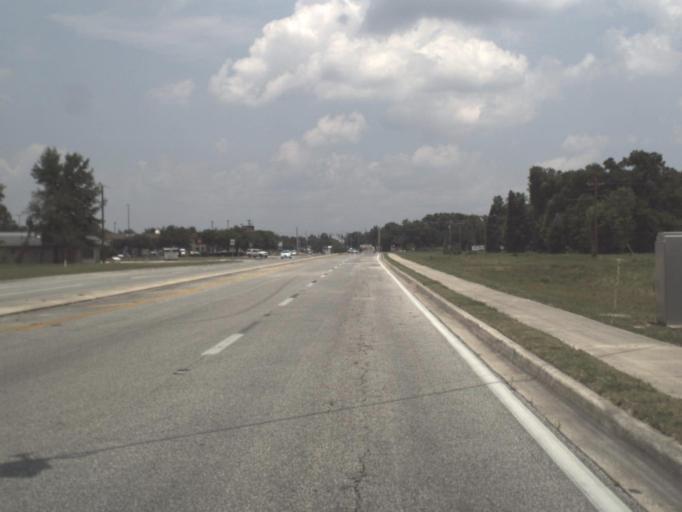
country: US
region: Florida
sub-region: Putnam County
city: Palatka
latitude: 29.6349
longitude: -81.6816
